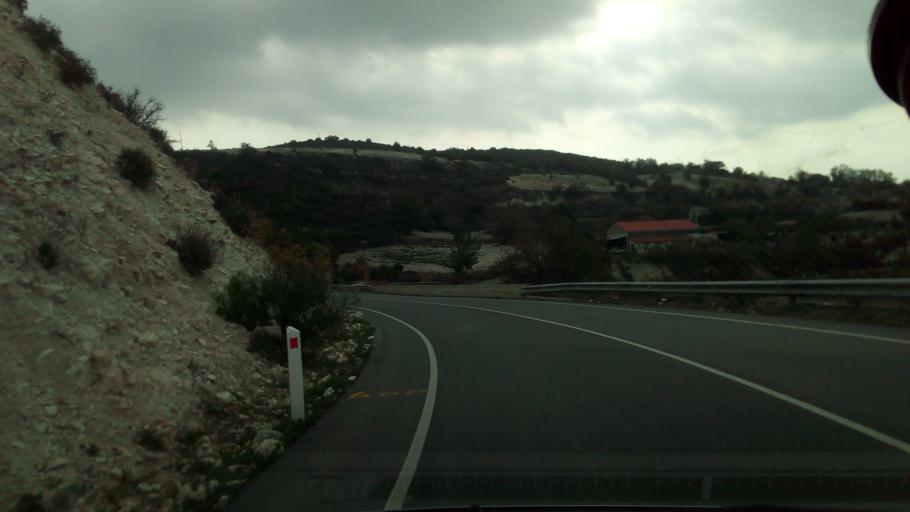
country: CY
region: Lefkosia
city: Lythrodontas
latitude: 34.8711
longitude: 33.2890
